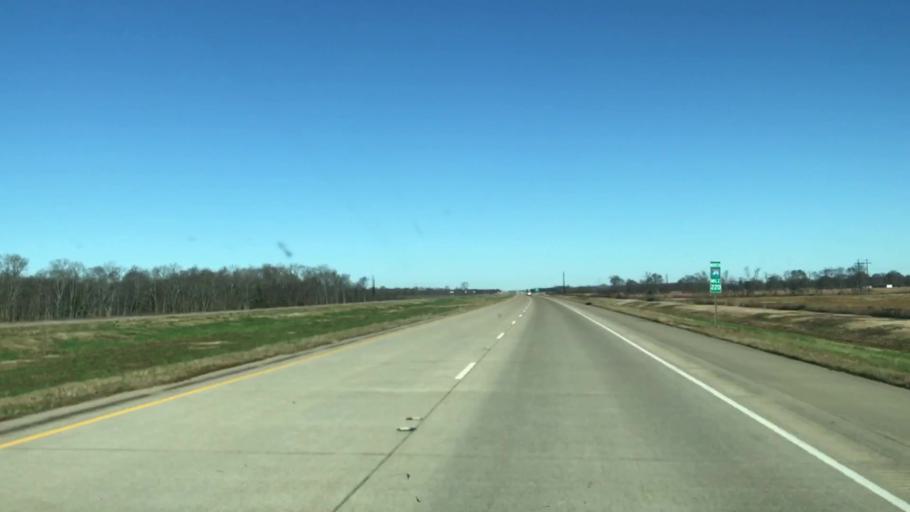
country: US
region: Louisiana
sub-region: Caddo Parish
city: Blanchard
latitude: 32.6567
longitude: -93.8426
